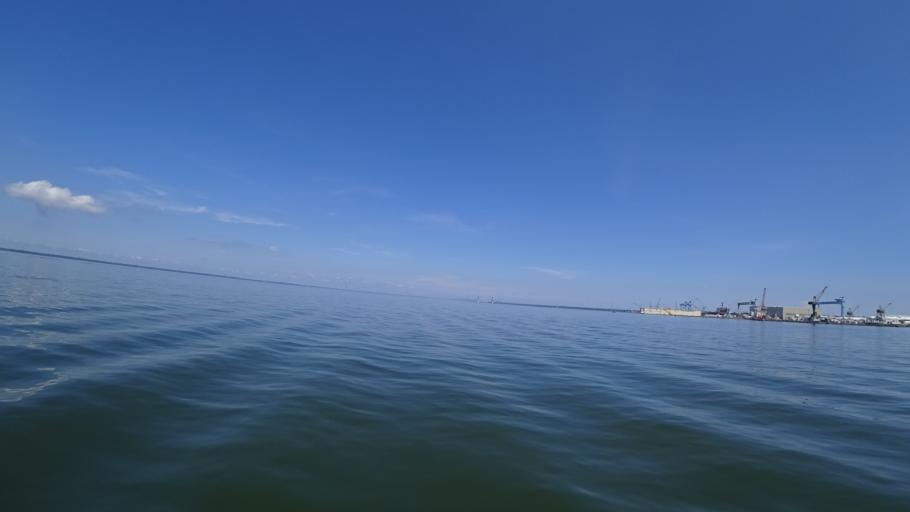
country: US
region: Virginia
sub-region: City of Newport News
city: Newport News
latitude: 36.9777
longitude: -76.4444
